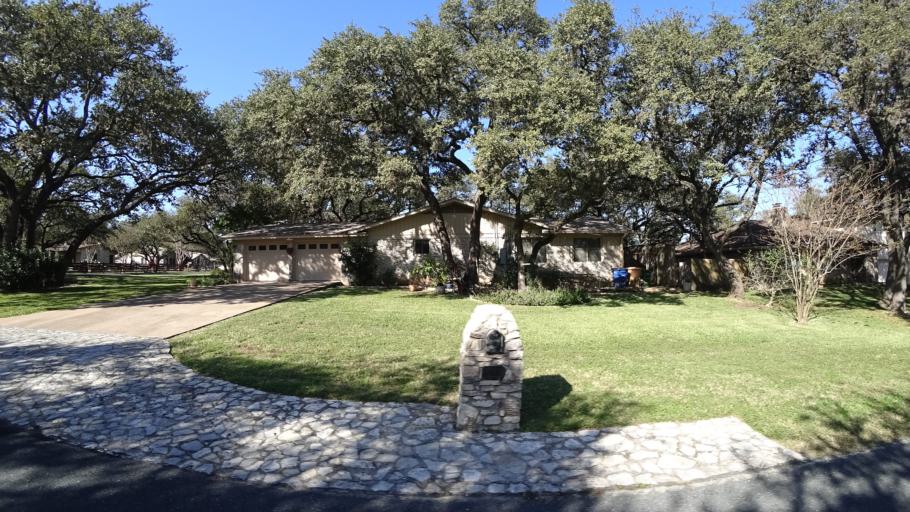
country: US
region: Texas
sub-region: Travis County
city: Barton Creek
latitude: 30.2305
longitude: -97.8712
